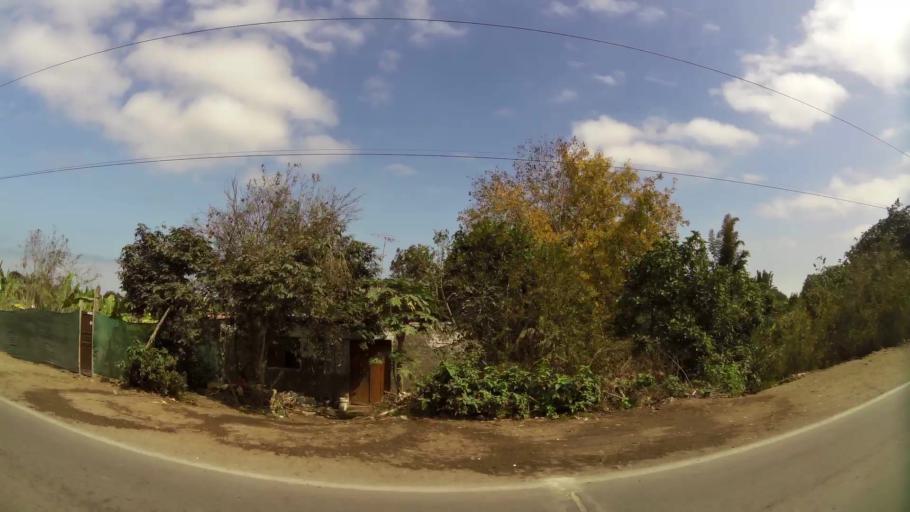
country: PE
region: Lima
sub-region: Provincia de Canete
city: Mala
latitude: -12.6814
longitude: -76.6278
